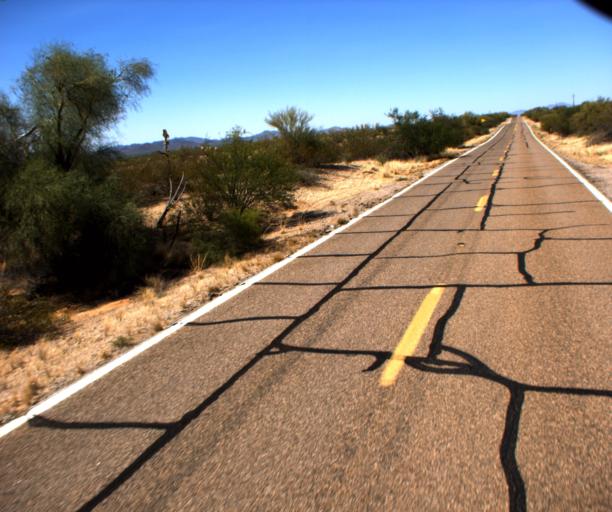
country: US
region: Arizona
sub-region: Pima County
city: Three Points
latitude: 31.9797
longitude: -111.3760
